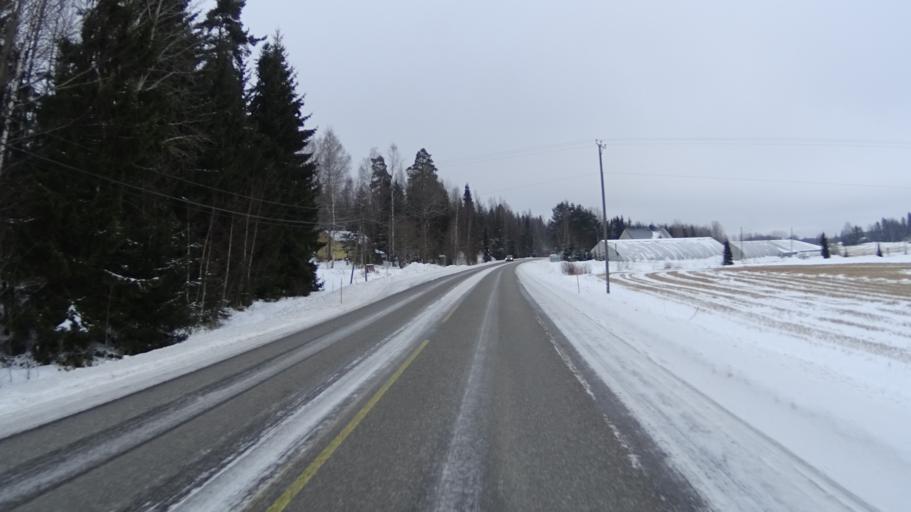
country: FI
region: Uusimaa
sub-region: Helsinki
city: Karkkila
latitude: 60.5155
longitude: 24.1770
